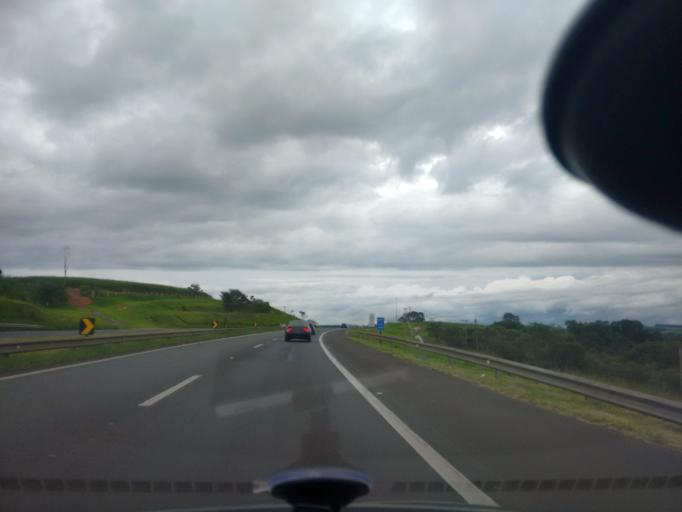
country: BR
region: Sao Paulo
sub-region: Rio Claro
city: Rio Claro
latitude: -22.3450
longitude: -47.6514
